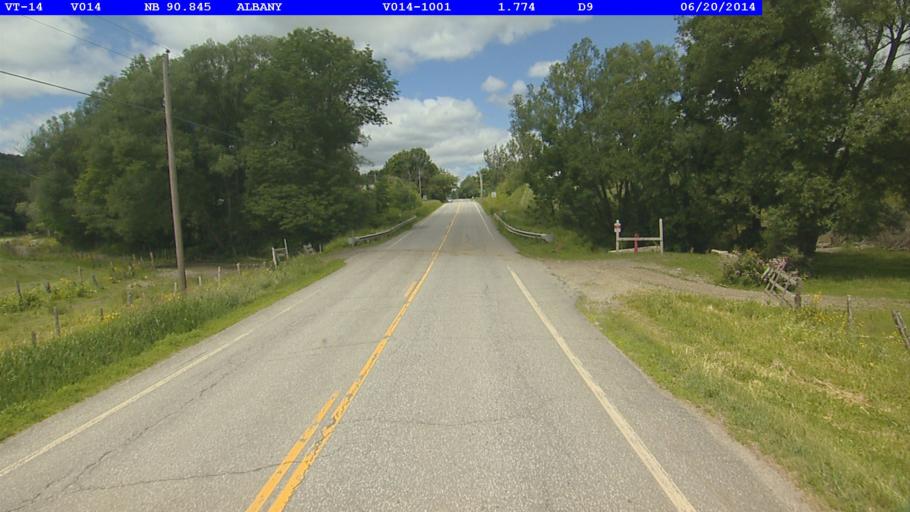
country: US
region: Vermont
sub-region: Caledonia County
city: Hardwick
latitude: 44.7269
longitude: -72.3818
